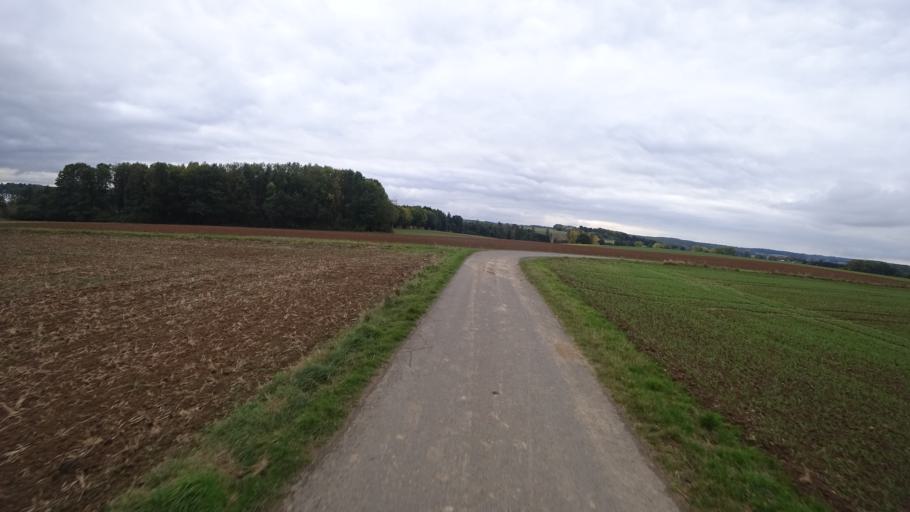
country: DE
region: Rheinland-Pfalz
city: Marienrachdorf
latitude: 50.5486
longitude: 7.6988
